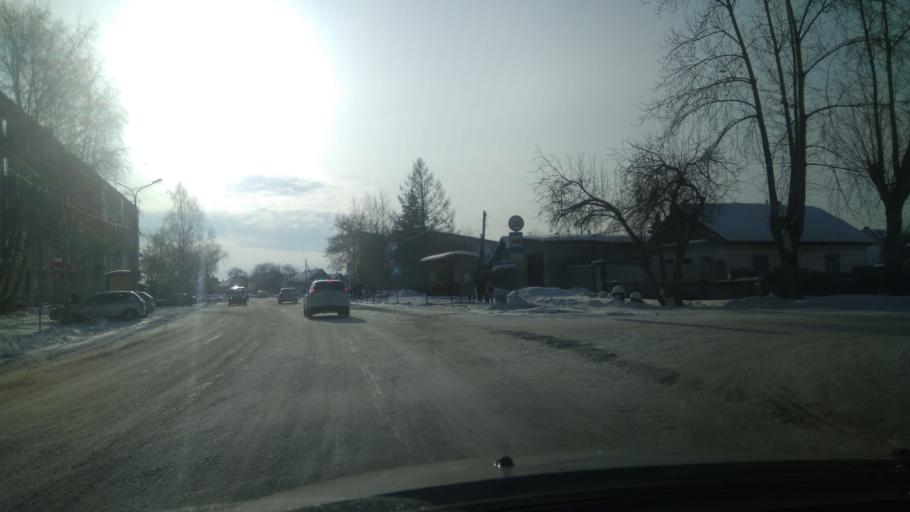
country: RU
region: Sverdlovsk
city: Sukhoy Log
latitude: 56.8976
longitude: 62.0312
